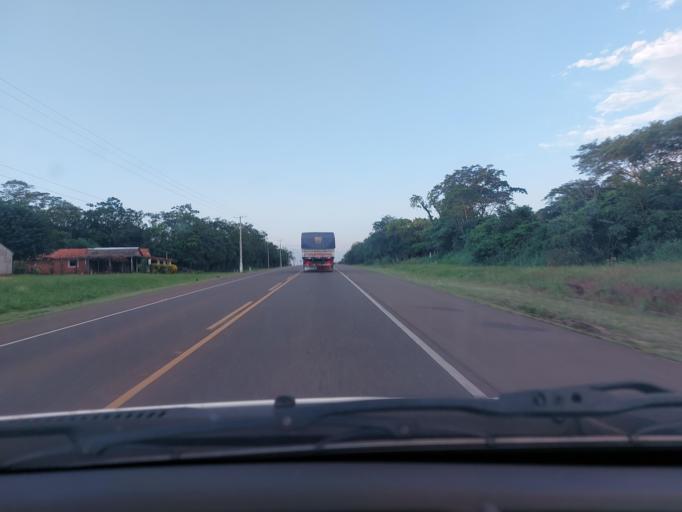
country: PY
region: San Pedro
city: Union
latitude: -24.7663
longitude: -56.6812
